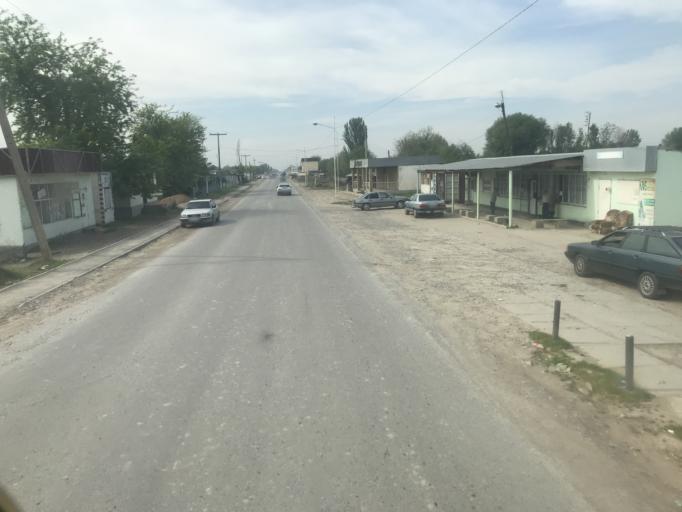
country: KZ
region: Ongtustik Qazaqstan
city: Asykata
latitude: 41.0073
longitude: 68.2155
